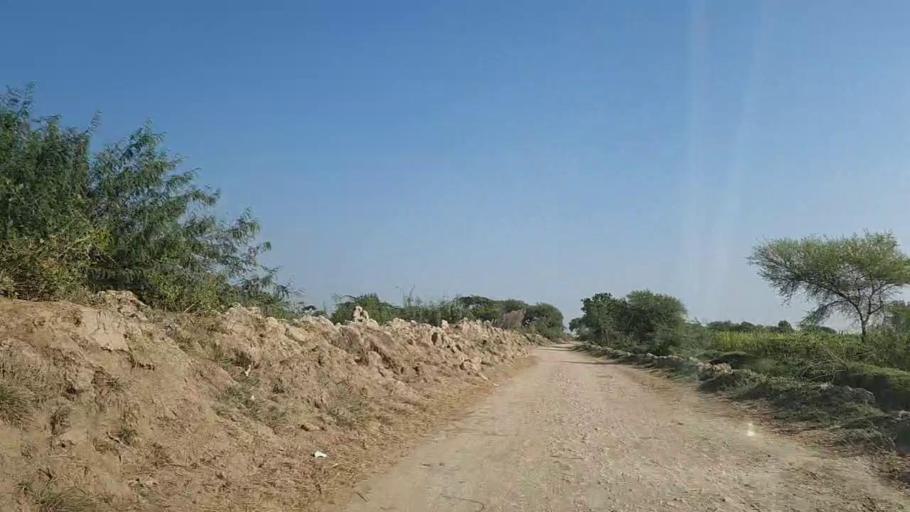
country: PK
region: Sindh
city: Chuhar Jamali
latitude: 24.5705
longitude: 68.0401
